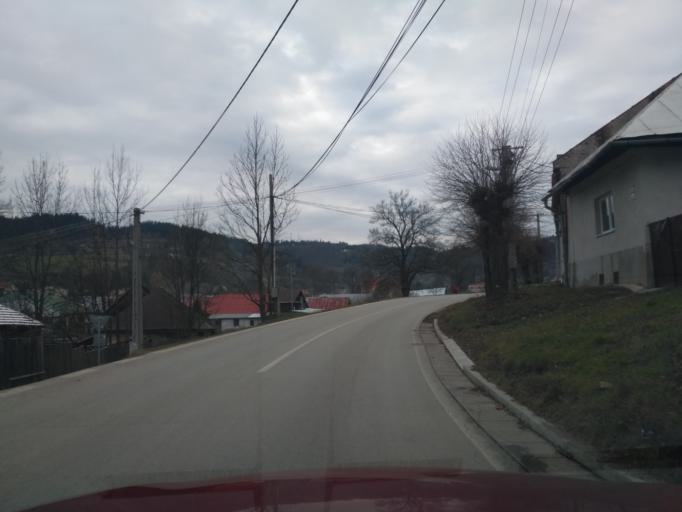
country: SK
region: Kosicky
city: Spisska Nova Ves
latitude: 48.8388
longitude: 20.6230
